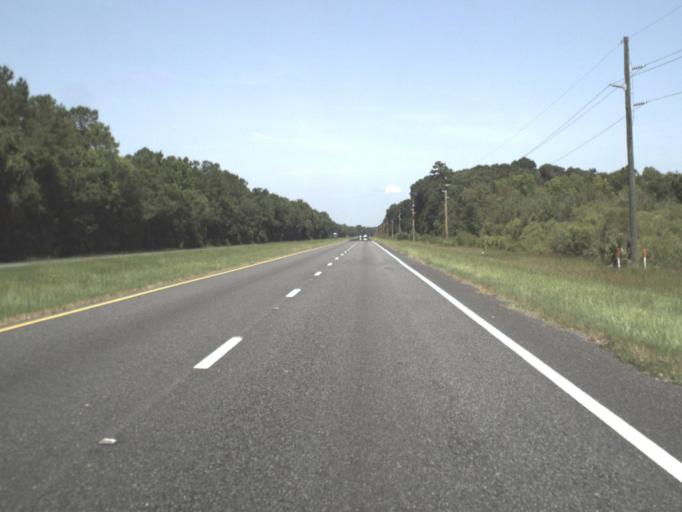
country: US
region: Florida
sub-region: Dixie County
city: Cross City
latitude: 29.6743
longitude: -83.2397
